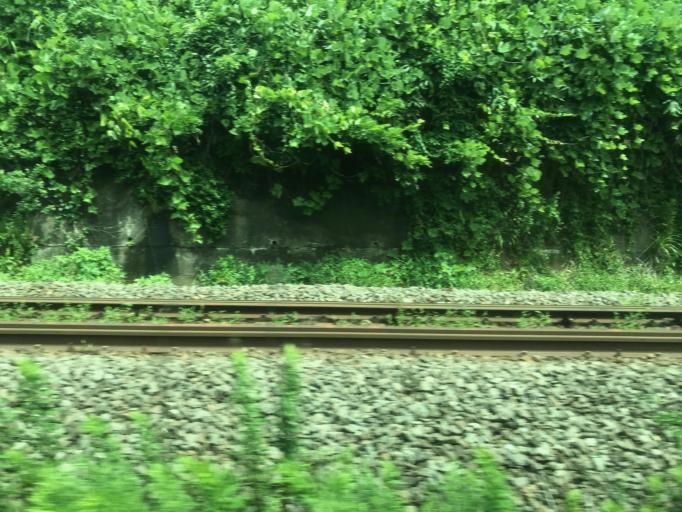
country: JP
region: Fukushima
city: Koriyama
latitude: 37.4532
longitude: 140.3818
